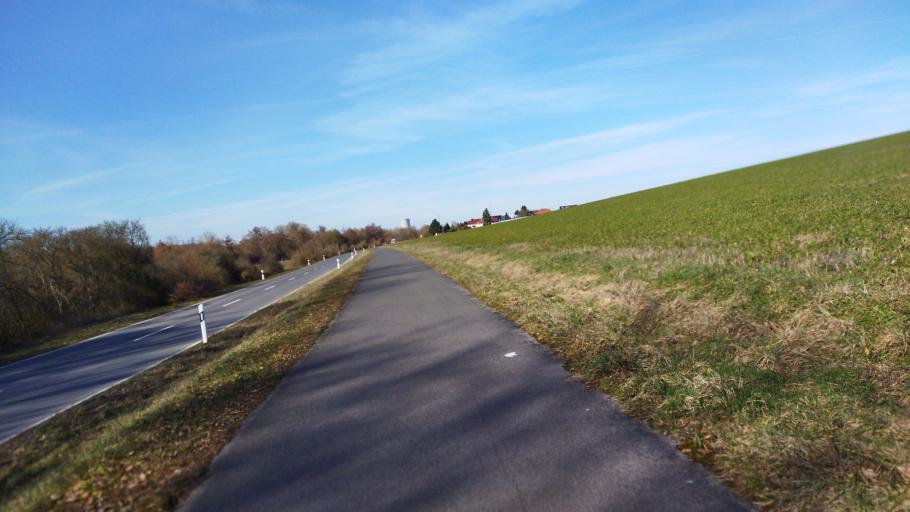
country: DE
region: Bavaria
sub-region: Regierungsbezirk Unterfranken
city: Wipfeld
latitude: 49.9357
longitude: 10.1825
